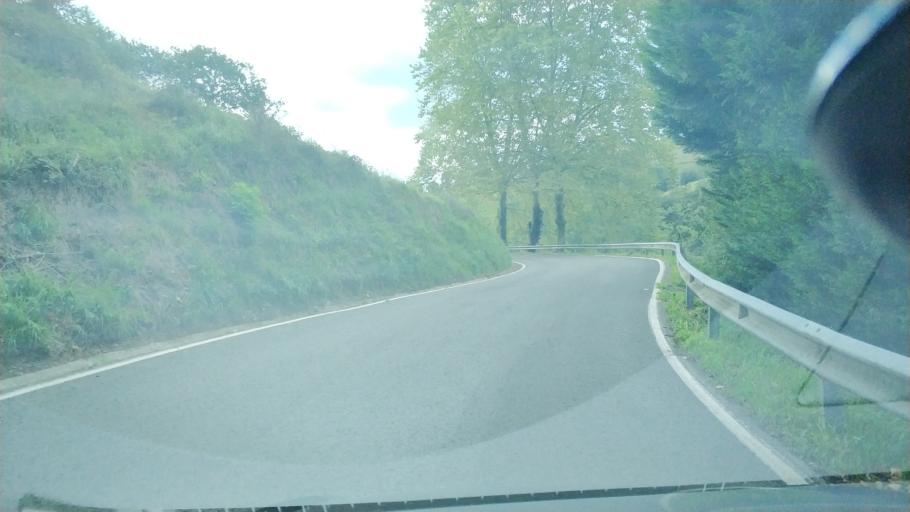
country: ES
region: Cantabria
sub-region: Provincia de Cantabria
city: Santa Maria de Cayon
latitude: 43.2892
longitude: -3.8228
